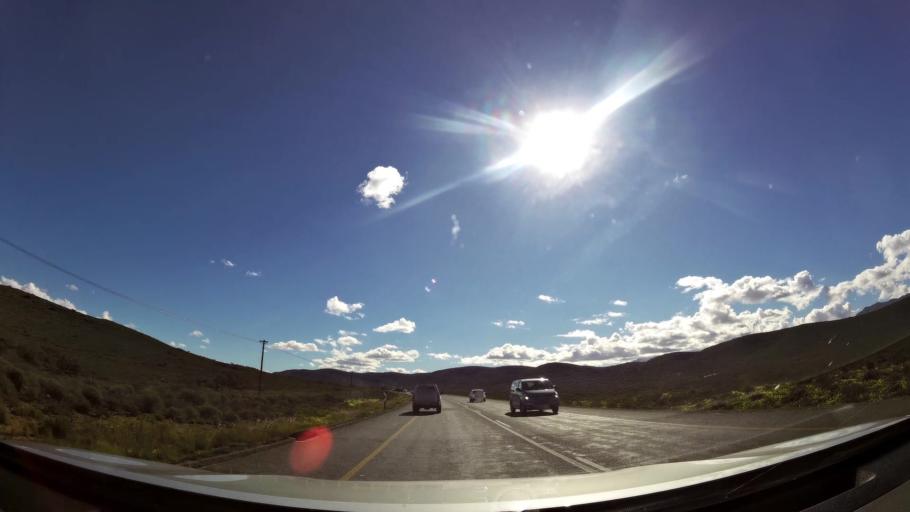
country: ZA
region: Western Cape
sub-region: Cape Winelands District Municipality
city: Worcester
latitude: -33.7406
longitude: 19.6927
